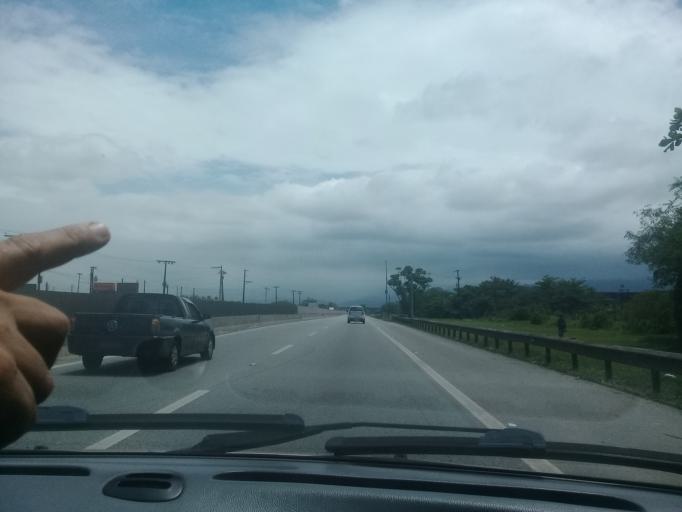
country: BR
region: Sao Paulo
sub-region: Guaruja
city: Guaruja
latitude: -23.9780
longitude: -46.2671
